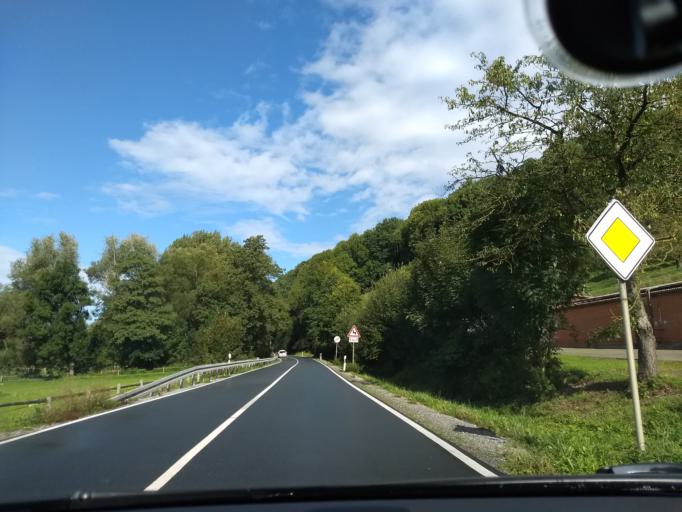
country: DE
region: North Rhine-Westphalia
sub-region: Regierungsbezirk Detmold
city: Buren
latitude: 51.5246
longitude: 8.5332
